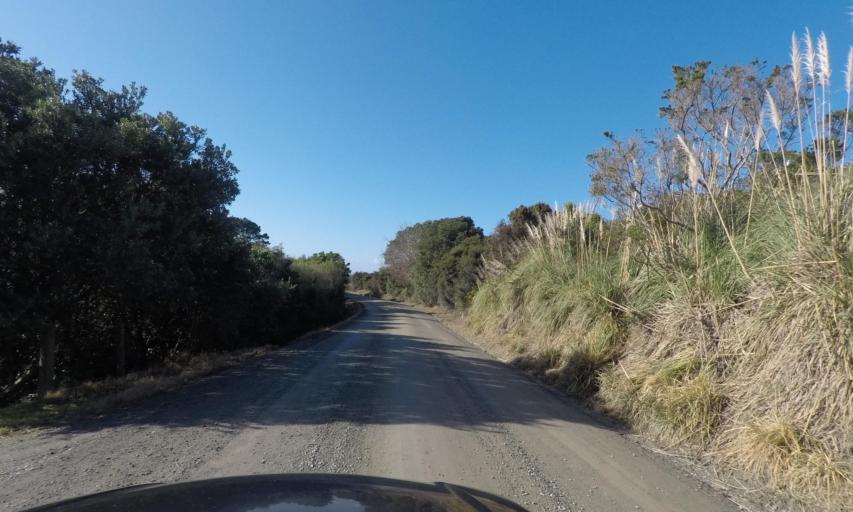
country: NZ
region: Auckland
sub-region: Auckland
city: Wellsford
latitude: -36.1414
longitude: 174.5912
